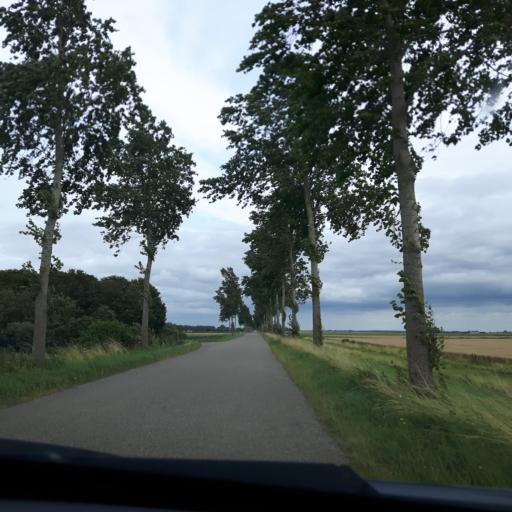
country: NL
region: Zeeland
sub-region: Gemeente Noord-Beveland
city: Kamperland
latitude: 51.5646
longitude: 3.7092
